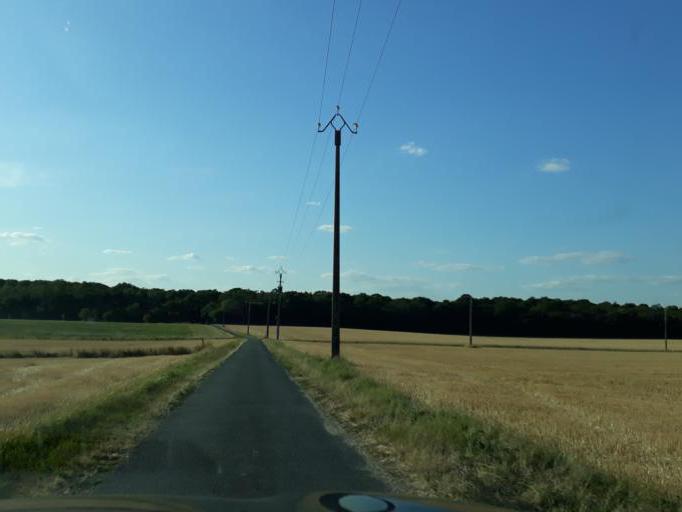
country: FR
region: Centre
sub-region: Departement du Loiret
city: Chaingy
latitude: 47.9054
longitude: 1.7580
